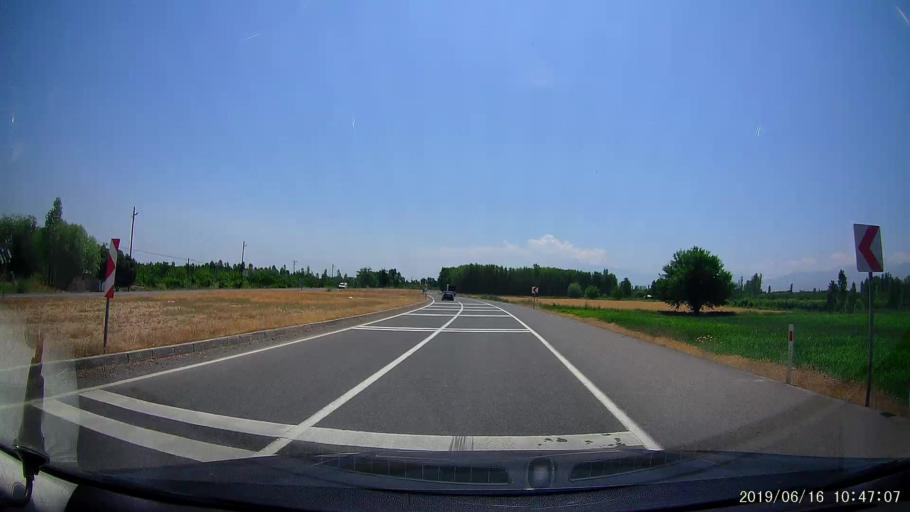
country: AM
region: Armavir
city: Shenavan
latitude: 40.0148
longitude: 43.8851
